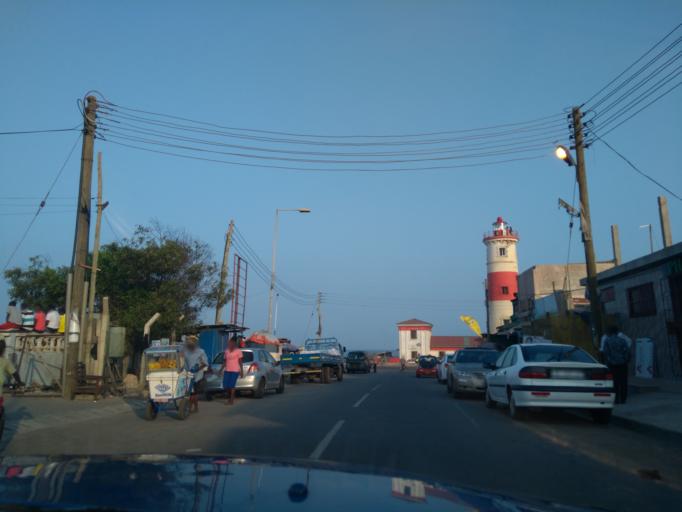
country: GH
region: Greater Accra
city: Accra
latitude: 5.5338
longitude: -0.2125
